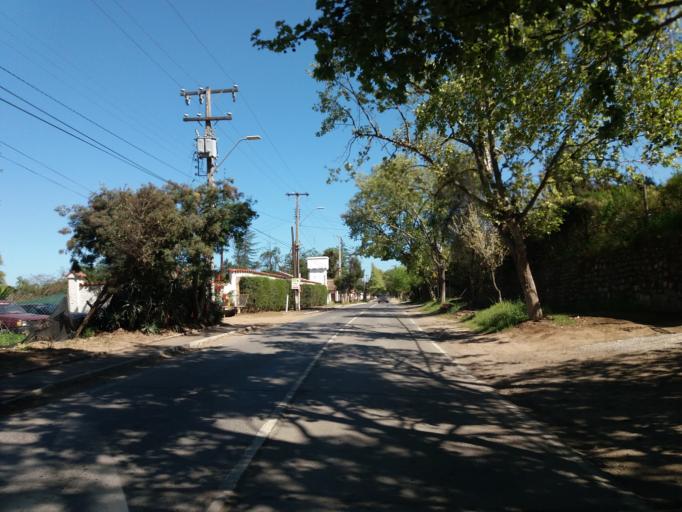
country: CL
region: Valparaiso
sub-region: Provincia de Marga Marga
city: Limache
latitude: -33.0004
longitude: -71.2105
